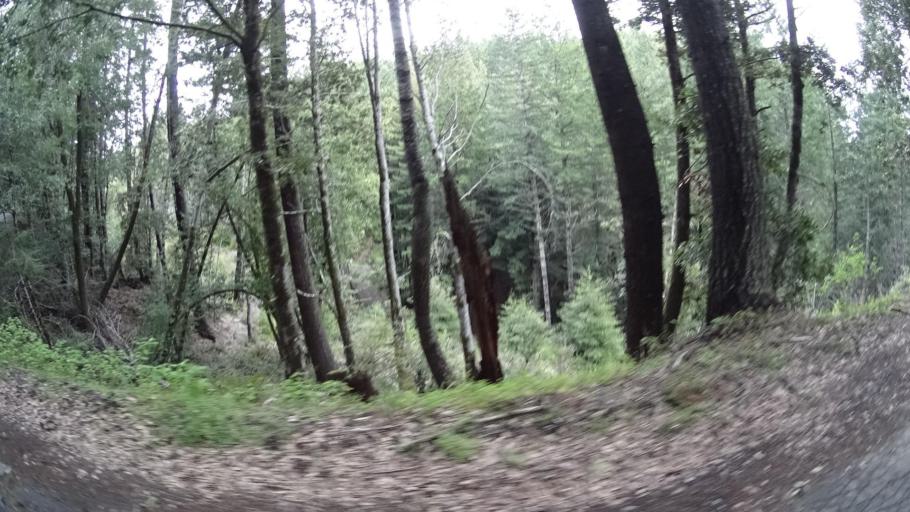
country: US
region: California
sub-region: Humboldt County
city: Blue Lake
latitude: 40.8614
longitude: -123.9102
